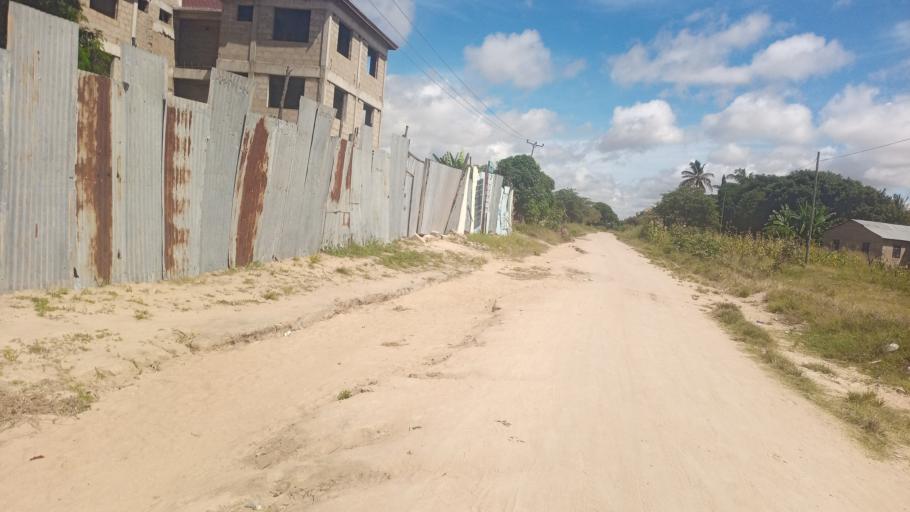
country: TZ
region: Dodoma
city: Dodoma
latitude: -6.1951
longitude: 35.7260
